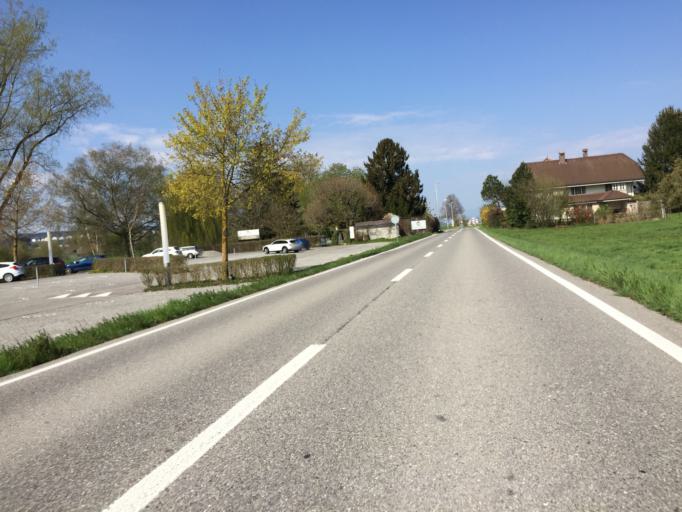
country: CH
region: Bern
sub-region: Bern-Mittelland District
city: Munchenbuchsee
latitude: 47.0291
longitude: 7.4619
